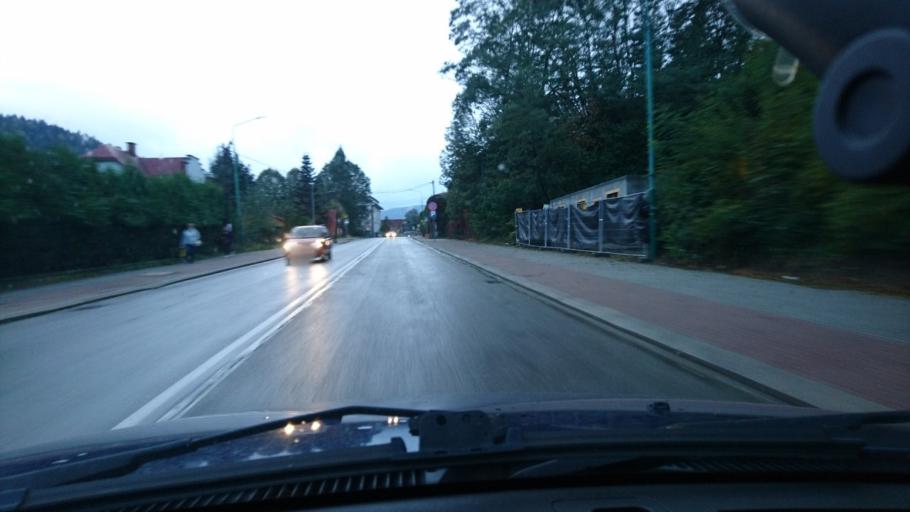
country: PL
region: Silesian Voivodeship
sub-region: Powiat bielski
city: Szczyrk
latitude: 49.7192
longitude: 19.0377
